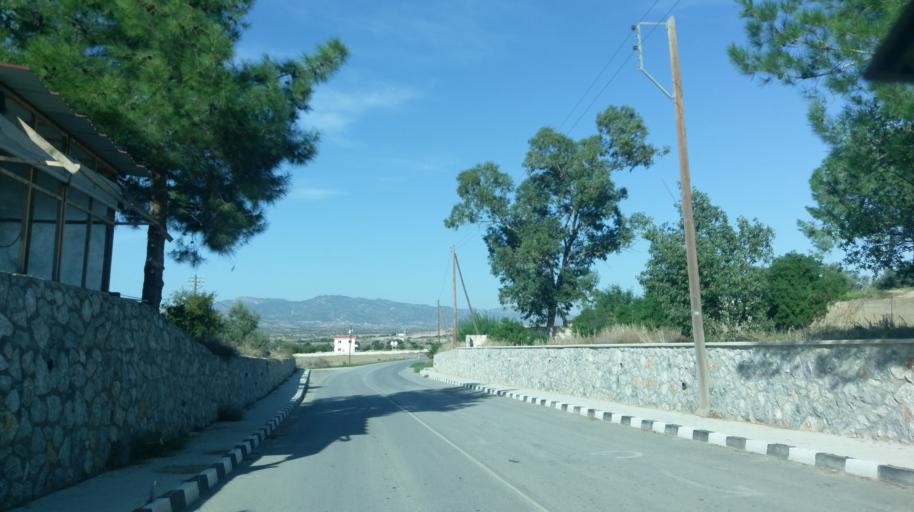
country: CY
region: Ammochostos
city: Trikomo
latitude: 35.2894
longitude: 33.8916
